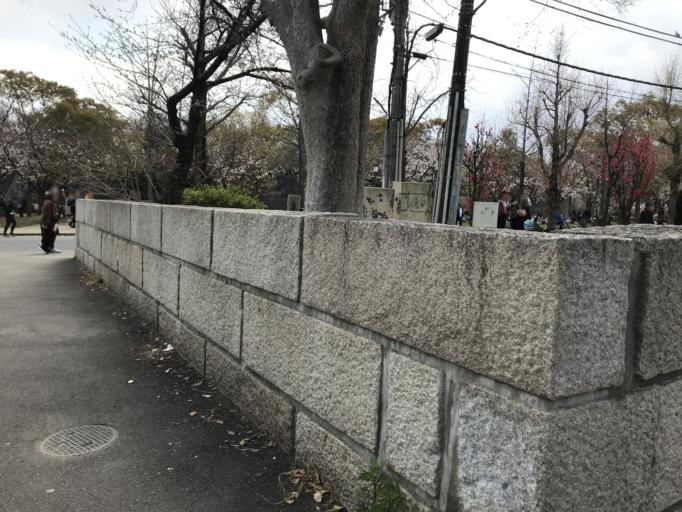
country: JP
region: Osaka
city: Osaka-shi
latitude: 34.6906
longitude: 135.5274
